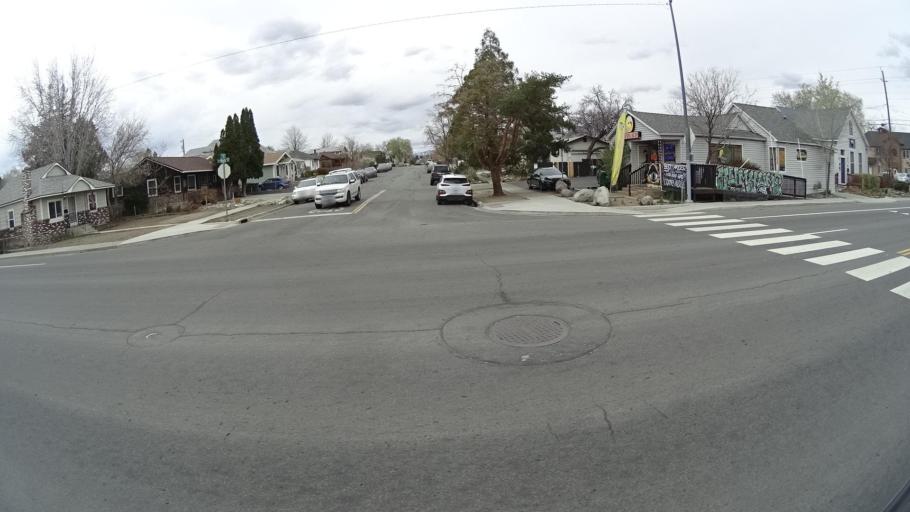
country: US
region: Nevada
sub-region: Washoe County
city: Sparks
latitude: 39.5398
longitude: -119.7654
